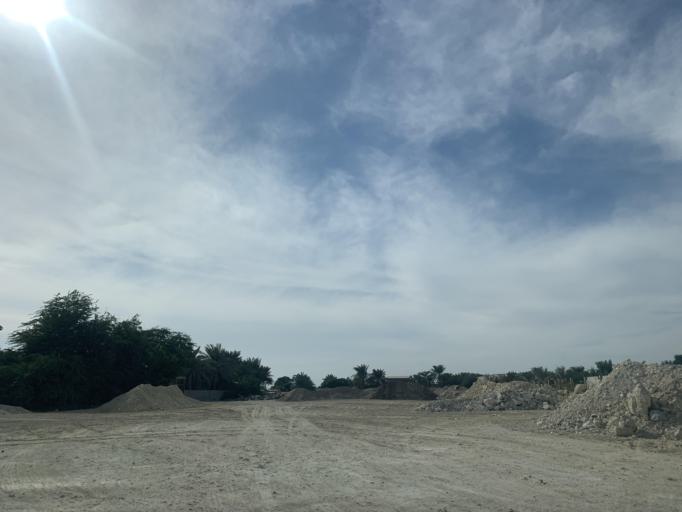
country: BH
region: Central Governorate
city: Madinat Hamad
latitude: 26.1225
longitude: 50.4695
